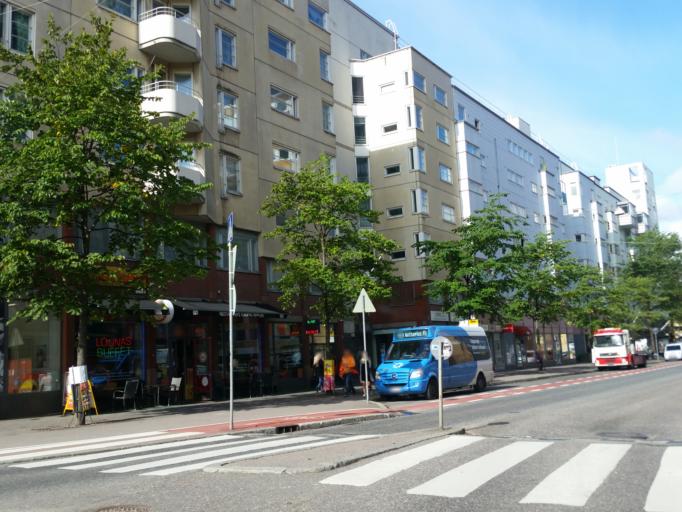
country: FI
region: Uusimaa
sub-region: Helsinki
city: Helsinki
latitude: 60.1686
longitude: 24.9291
